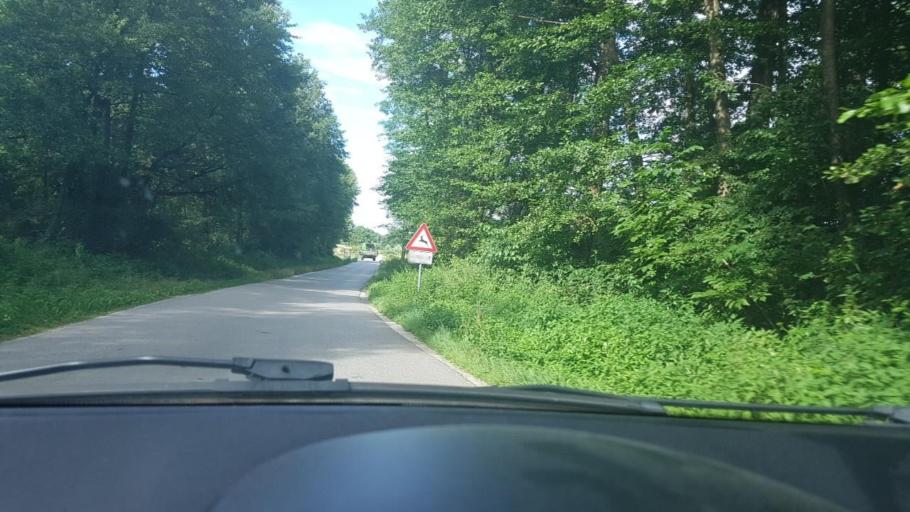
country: HR
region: Varazdinska
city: Tuzno
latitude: 46.2635
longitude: 16.1878
